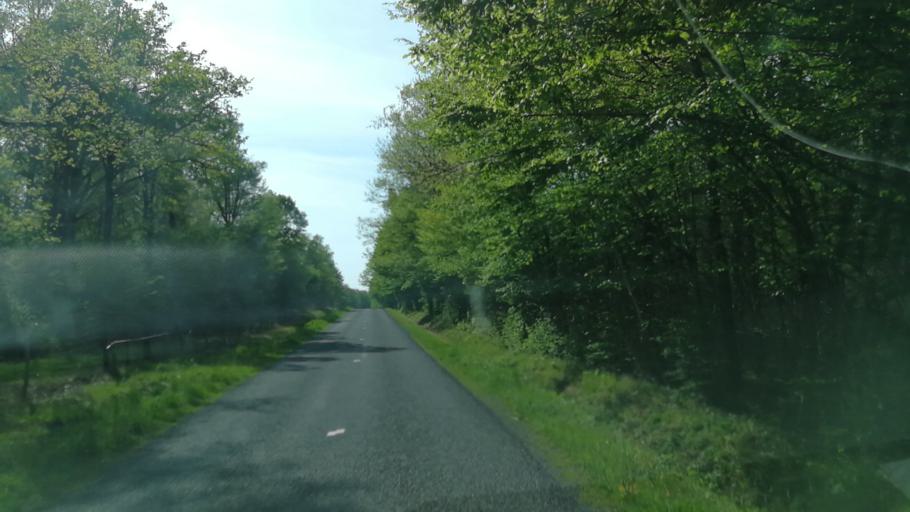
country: FR
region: Auvergne
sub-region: Departement de l'Allier
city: Neuilly-le-Real
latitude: 46.5061
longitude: 3.4759
